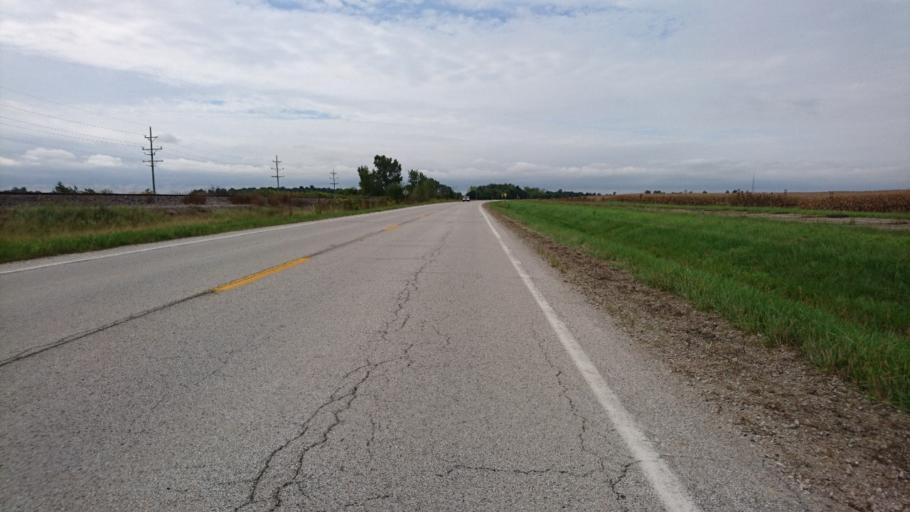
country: US
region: Illinois
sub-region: Livingston County
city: Odell
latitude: 41.0200
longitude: -88.5098
